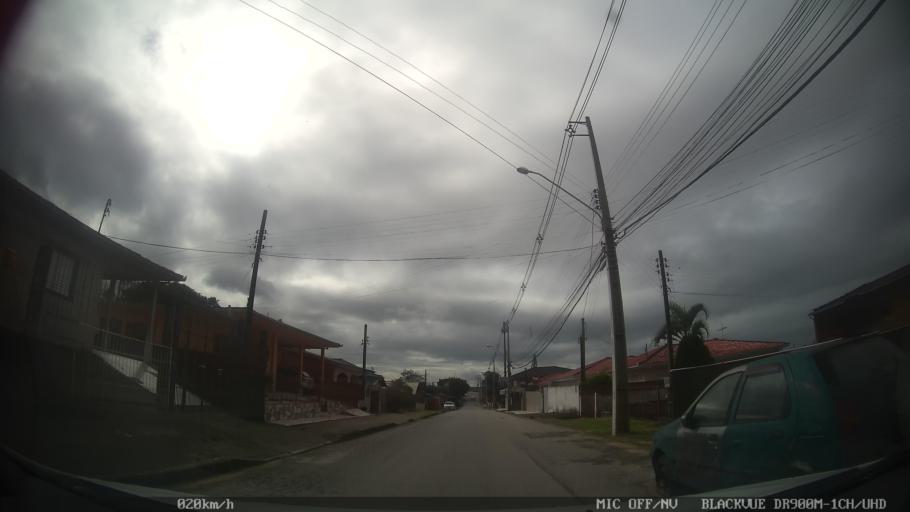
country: BR
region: Santa Catarina
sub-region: Biguacu
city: Biguacu
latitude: -27.5415
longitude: -48.6487
